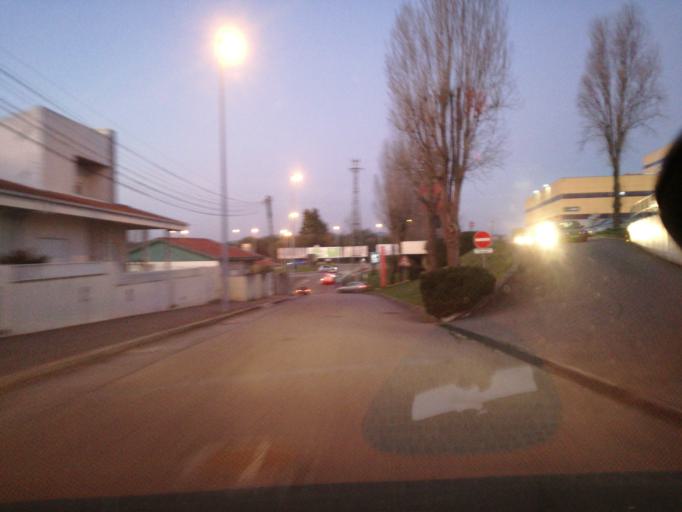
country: PT
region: Porto
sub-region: Valongo
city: Ermesinde
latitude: 41.2201
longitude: -8.5637
